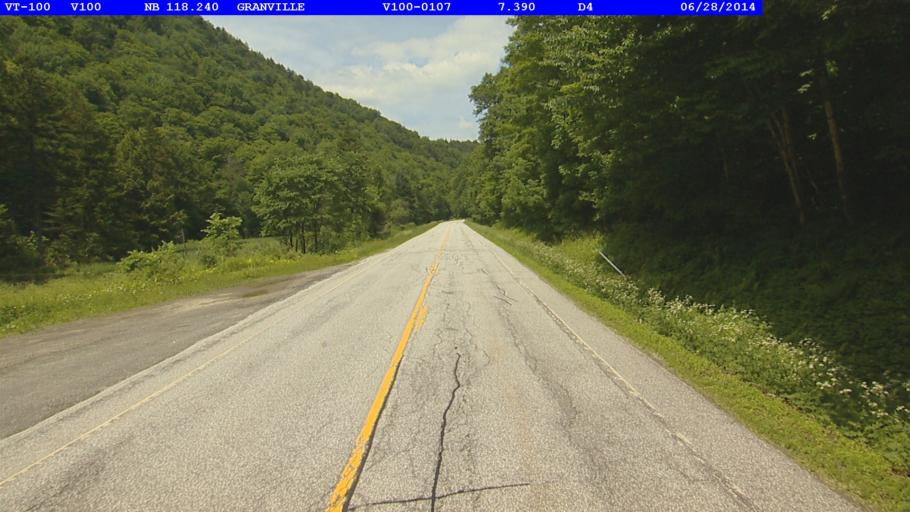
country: US
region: Vermont
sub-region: Orange County
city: Randolph
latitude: 44.0369
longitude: -72.8317
